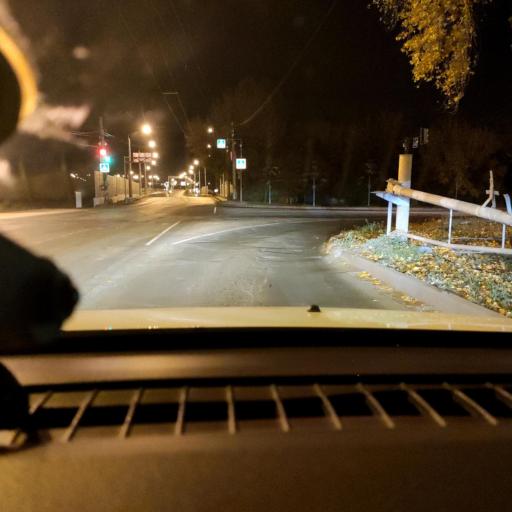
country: RU
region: Samara
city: Rozhdestveno
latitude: 53.1652
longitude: 50.0758
